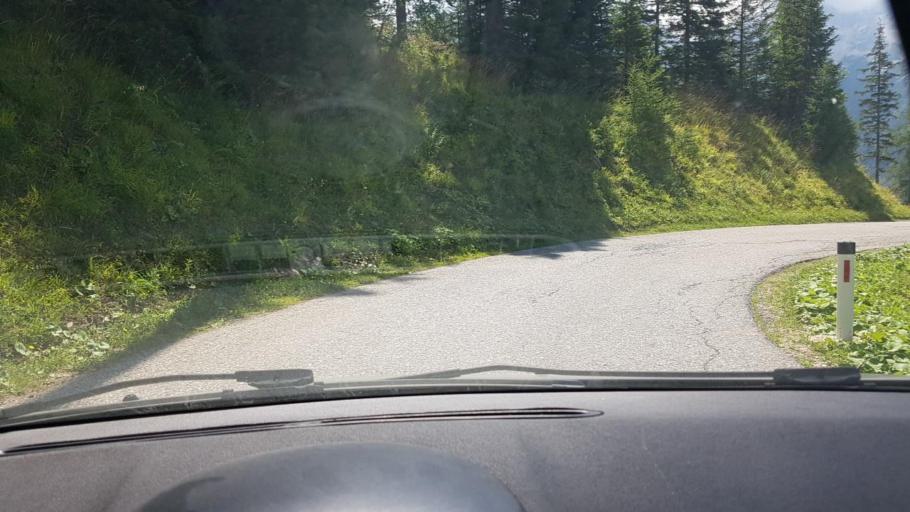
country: SI
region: Jezersko
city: Zgornje Jezersko
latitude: 46.4188
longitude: 14.5729
